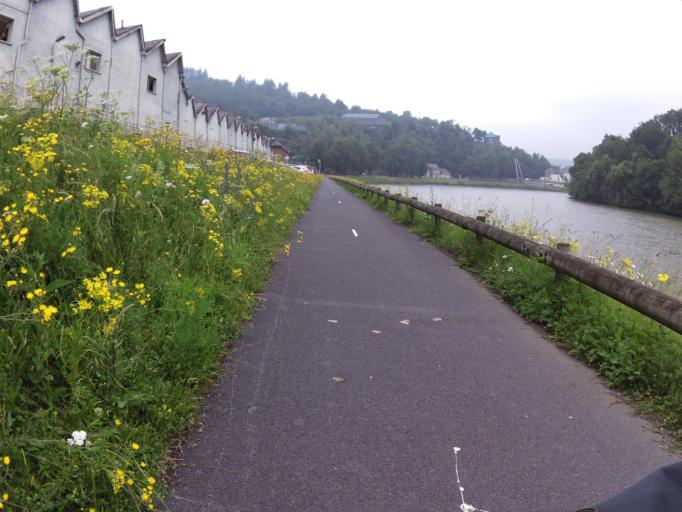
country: FR
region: Champagne-Ardenne
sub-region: Departement des Ardennes
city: Fumay
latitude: 49.9872
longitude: 4.6946
